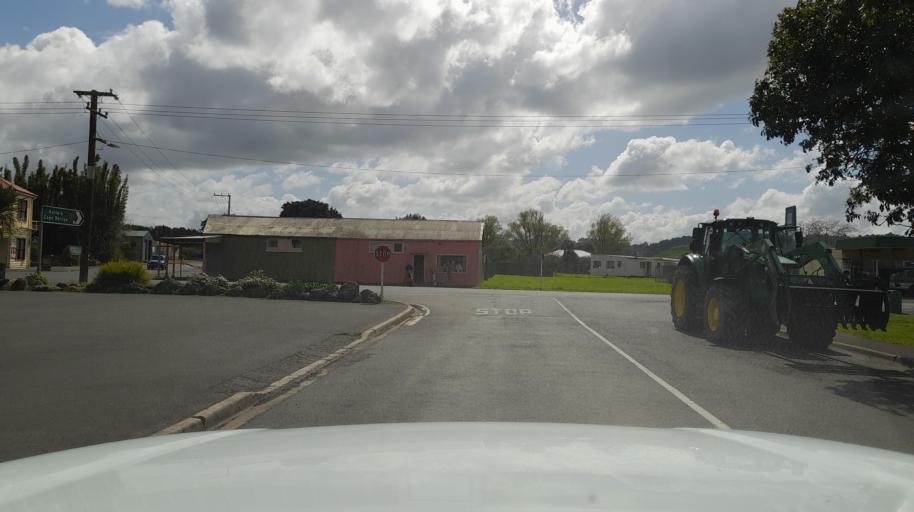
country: NZ
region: Northland
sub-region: Far North District
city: Waimate North
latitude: -35.3521
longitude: 173.8826
